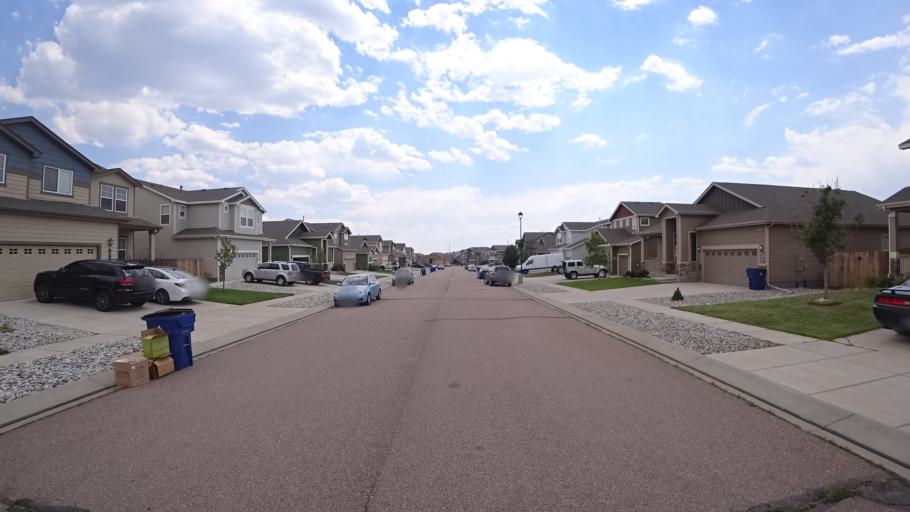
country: US
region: Colorado
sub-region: El Paso County
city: Black Forest
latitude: 38.9484
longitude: -104.7001
